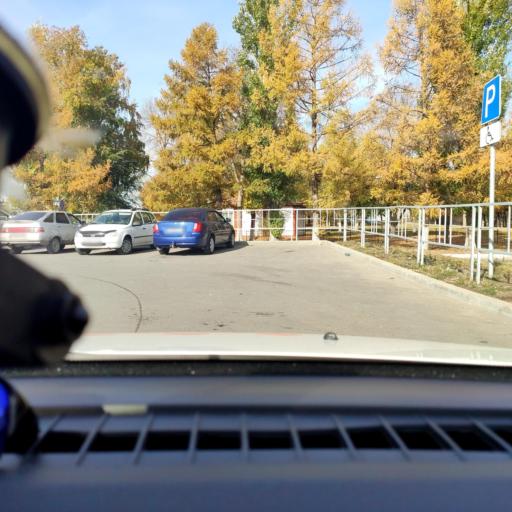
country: RU
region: Samara
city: Samara
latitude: 53.2594
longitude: 50.2432
